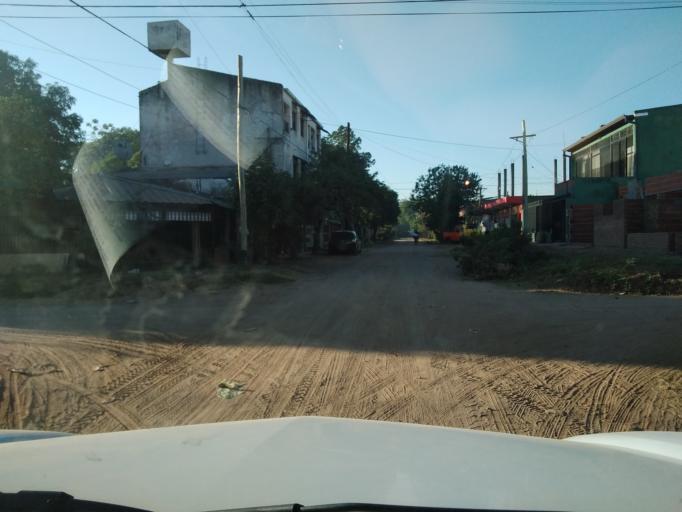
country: AR
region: Corrientes
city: Corrientes
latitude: -27.4782
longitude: -58.7862
